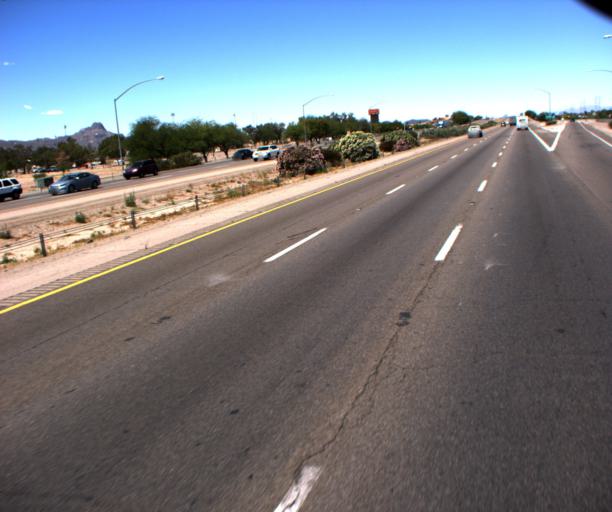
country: US
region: Arizona
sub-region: Pima County
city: Flowing Wells
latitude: 32.3326
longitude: -111.0608
